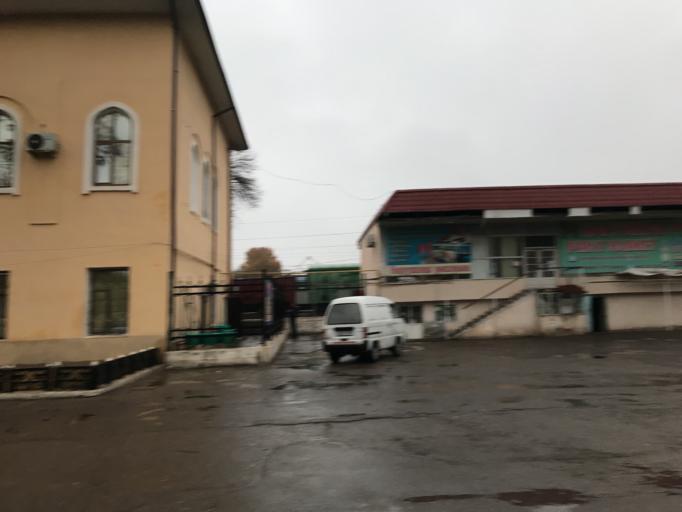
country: UZ
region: Toshkent
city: Yangiyul
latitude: 41.1169
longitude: 69.0600
